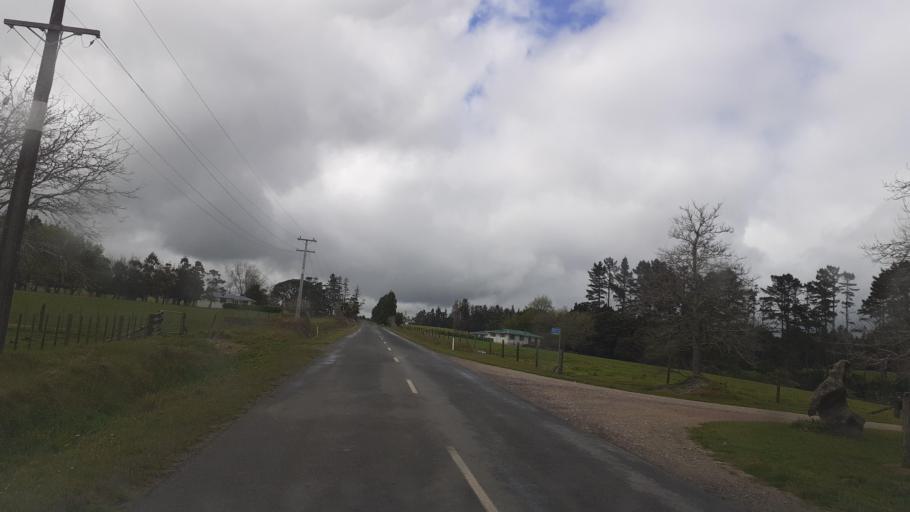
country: NZ
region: Northland
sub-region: Far North District
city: Waimate North
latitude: -35.2524
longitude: 173.7971
